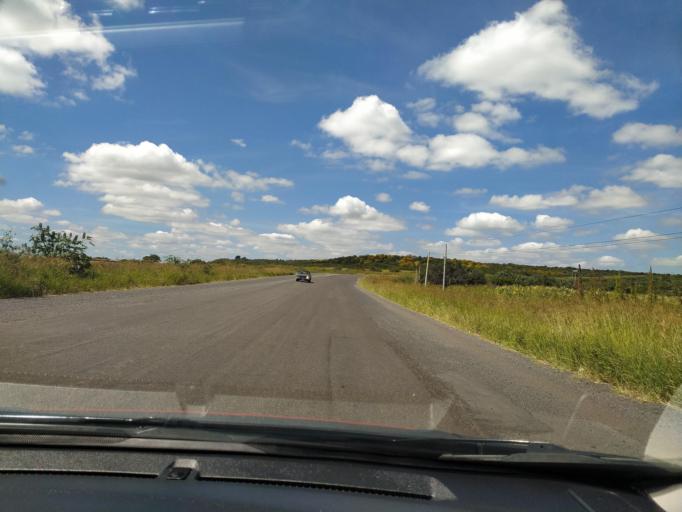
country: MX
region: Jalisco
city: San Diego de Alejandria
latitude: 20.9993
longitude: -102.0044
